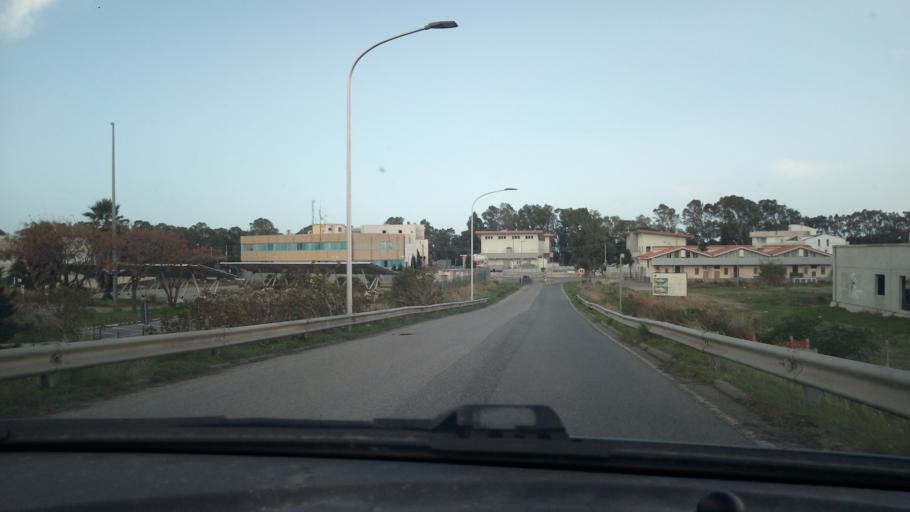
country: IT
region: Calabria
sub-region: Provincia di Catanzaro
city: Barone
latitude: 38.8327
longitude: 16.6386
